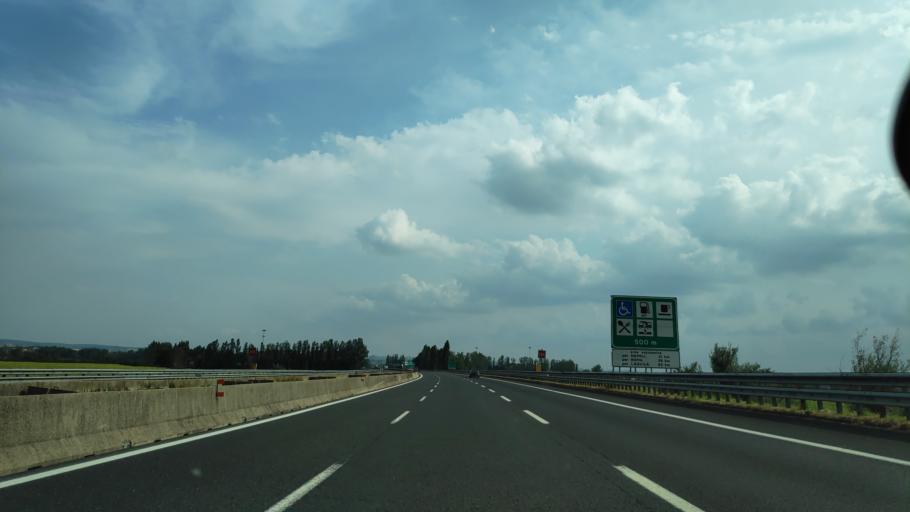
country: IT
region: Latium
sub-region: Citta metropolitana di Roma Capitale
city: Bivio di Capanelle
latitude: 42.1300
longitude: 12.6171
